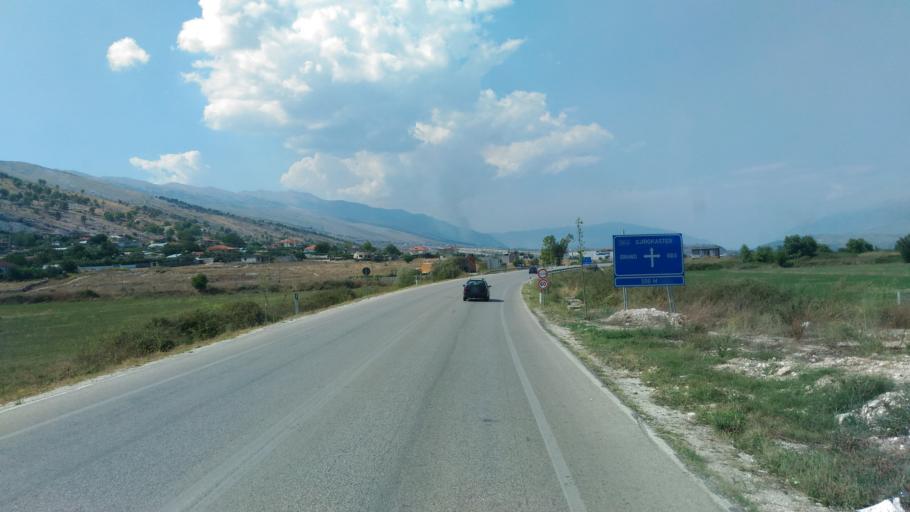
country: AL
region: Gjirokaster
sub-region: Rrethi i Gjirokastres
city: Dervician
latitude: 40.0158
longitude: 20.1972
